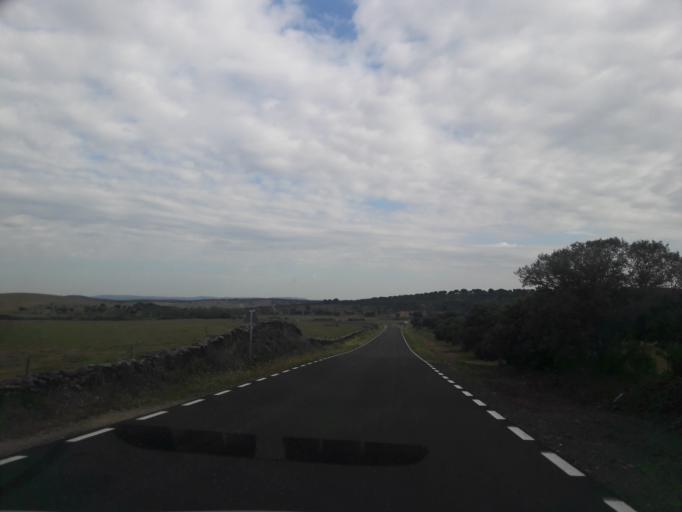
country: ES
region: Castille and Leon
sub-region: Provincia de Salamanca
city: Pastores
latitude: 40.5269
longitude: -6.5250
